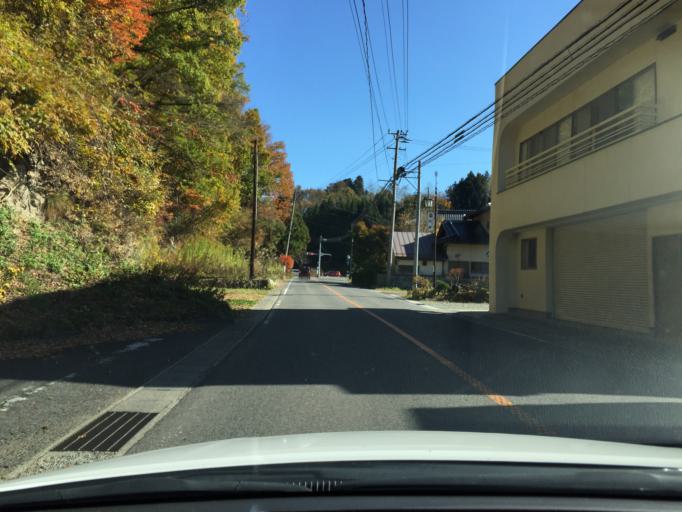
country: JP
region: Fukushima
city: Funehikimachi-funehiki
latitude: 37.4112
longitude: 140.5404
